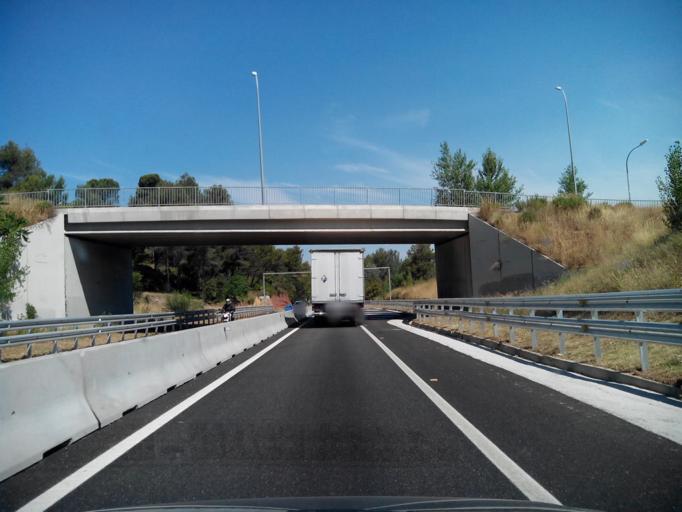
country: ES
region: Catalonia
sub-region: Provincia de Barcelona
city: Monistrol de Montserrat
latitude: 41.5967
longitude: 1.8953
